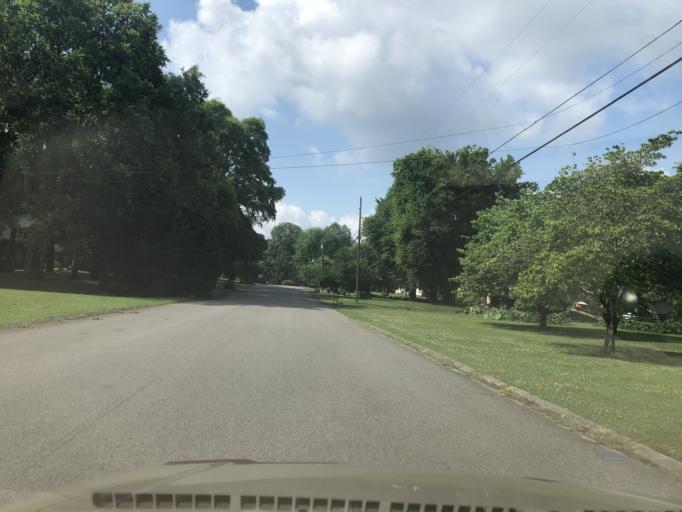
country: US
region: Tennessee
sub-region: Wilson County
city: Green Hill
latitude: 36.2344
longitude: -86.5846
